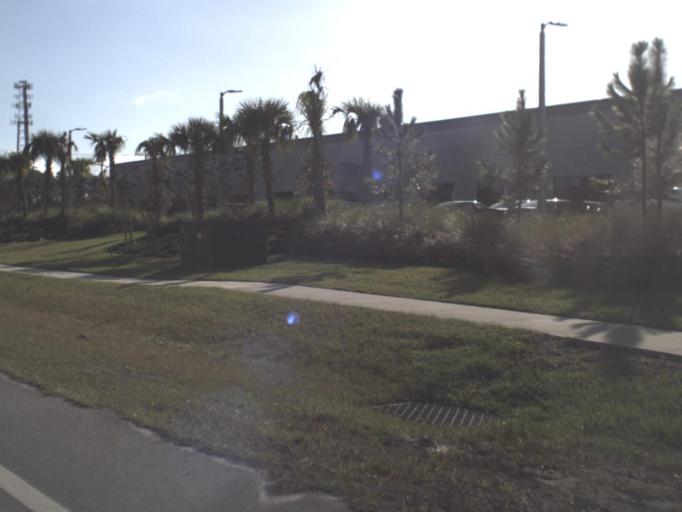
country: US
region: Florida
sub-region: Volusia County
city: Holly Hill
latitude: 29.2086
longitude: -81.0892
